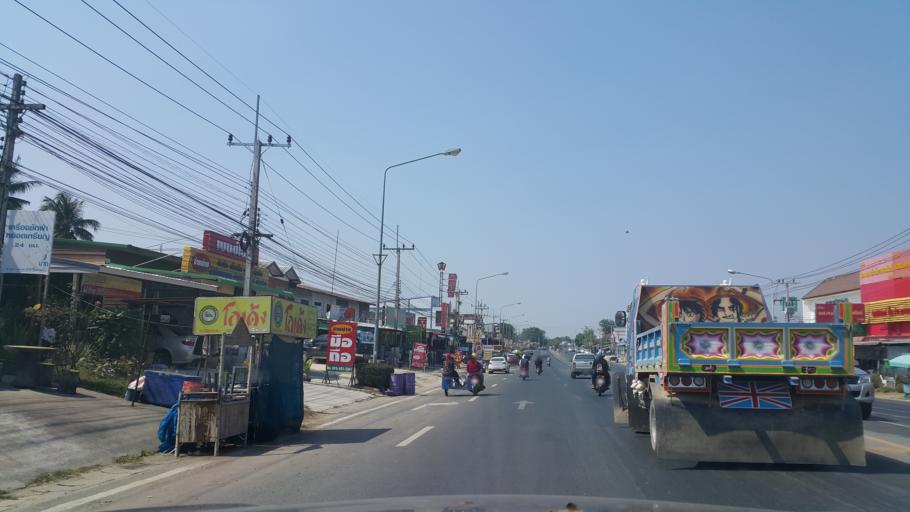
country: TH
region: Nakhon Ratchasima
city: Lam Thamen Chai
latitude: 15.3552
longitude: 102.9117
